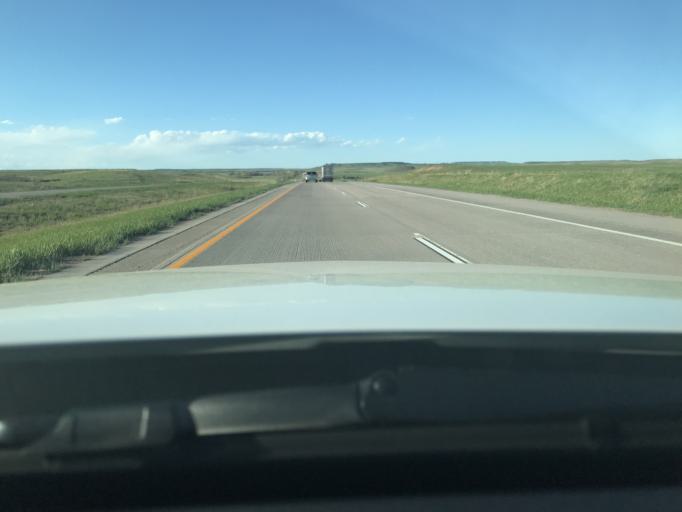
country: US
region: Wyoming
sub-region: Laramie County
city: South Greeley
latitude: 40.9322
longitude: -104.9298
